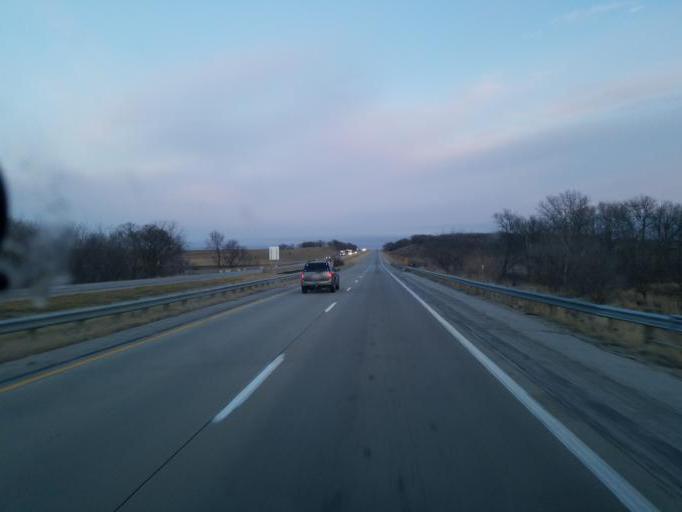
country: US
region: Iowa
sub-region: Pottawattamie County
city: Avoca
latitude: 41.4980
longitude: -95.3144
